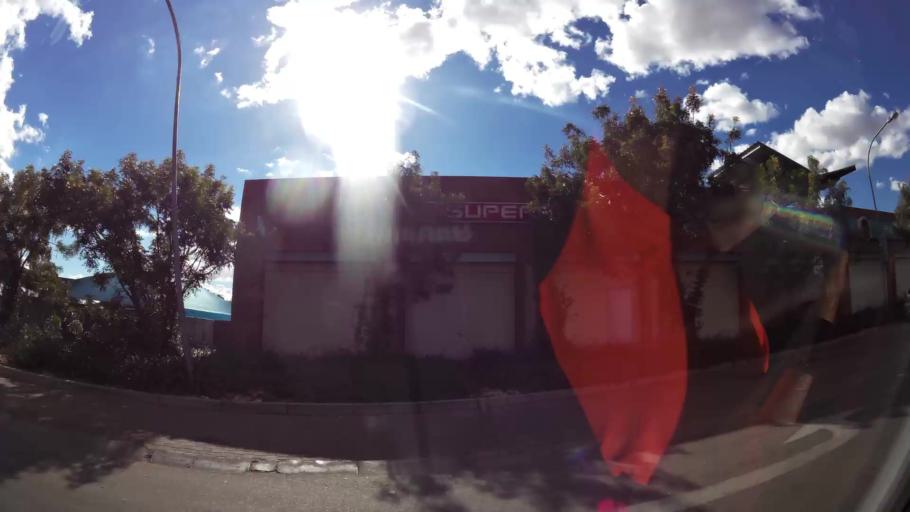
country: ZA
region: Limpopo
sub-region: Capricorn District Municipality
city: Polokwane
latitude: -23.8925
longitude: 29.4726
